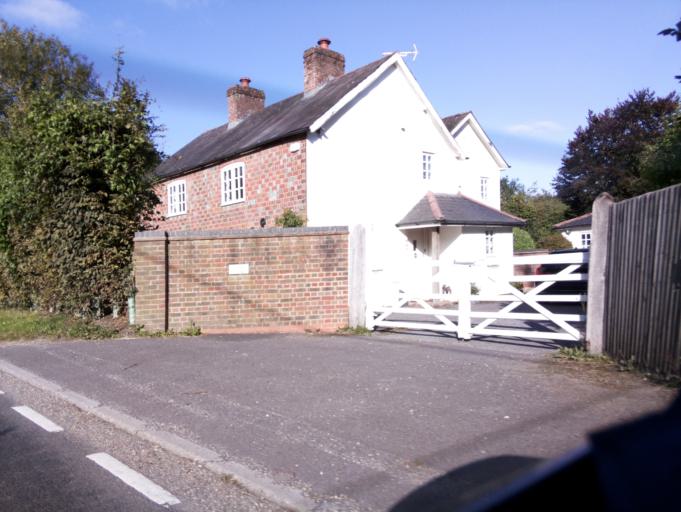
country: GB
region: England
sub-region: Hampshire
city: Alton
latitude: 51.1093
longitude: -0.9938
